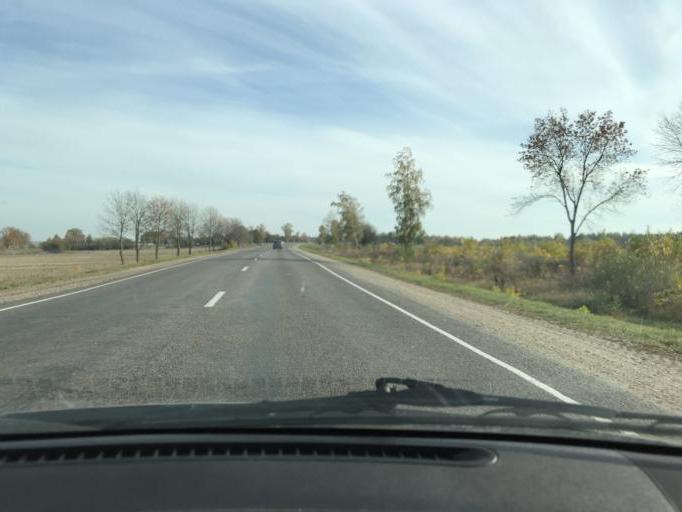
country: BY
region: Brest
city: Lahishyn
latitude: 52.2394
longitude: 26.0039
